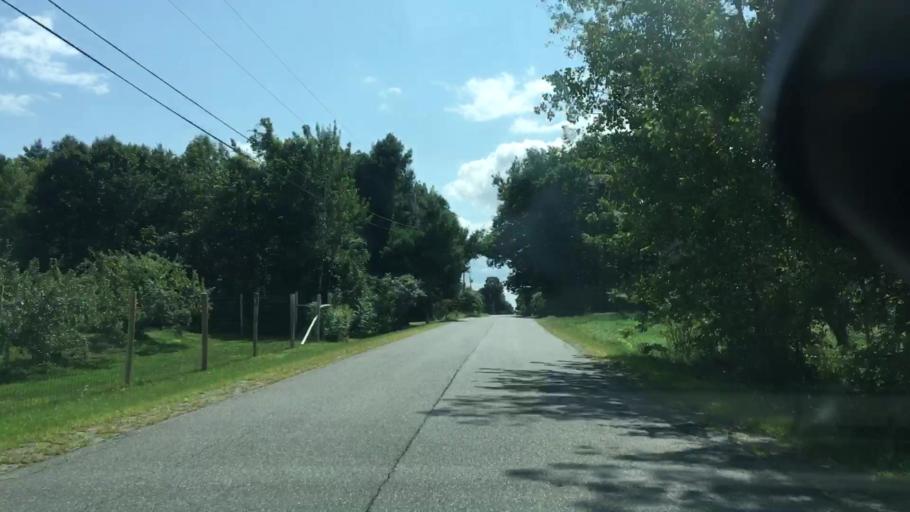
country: US
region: Maine
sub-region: Somerset County
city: Skowhegan
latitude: 44.6869
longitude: -69.6912
